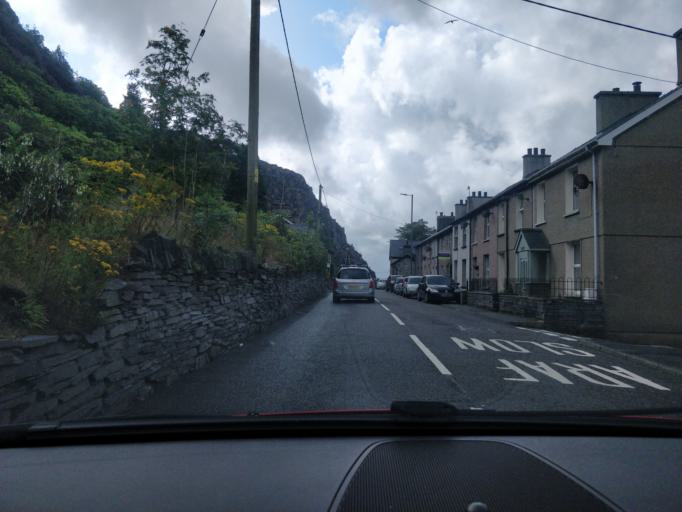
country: GB
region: Wales
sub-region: Gwynedd
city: Blaenau-Ffestiniog
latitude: 52.9998
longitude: -3.9427
